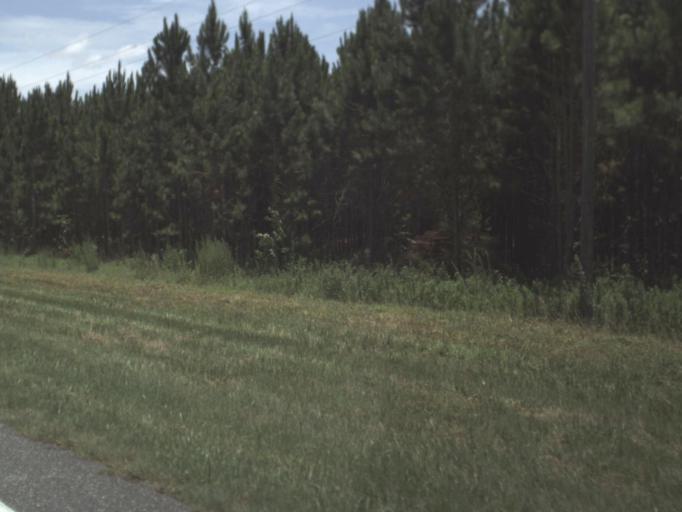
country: US
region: Florida
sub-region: Lafayette County
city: Mayo
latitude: 30.1722
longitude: -83.1491
